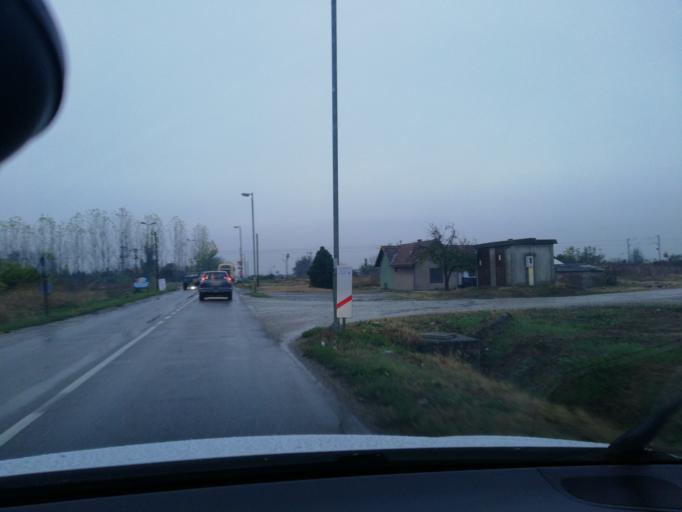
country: RS
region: Autonomna Pokrajina Vojvodina
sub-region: Sremski Okrug
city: Ruma
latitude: 44.9904
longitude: 19.8163
